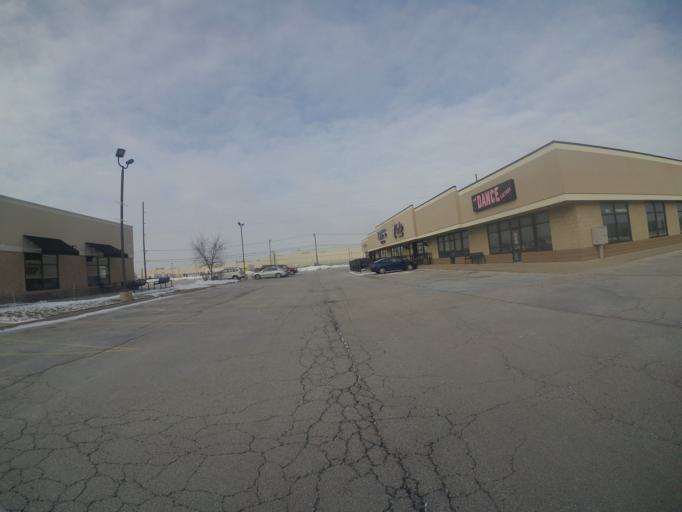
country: US
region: Ohio
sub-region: Wood County
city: Rossford
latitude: 41.5626
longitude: -83.5444
